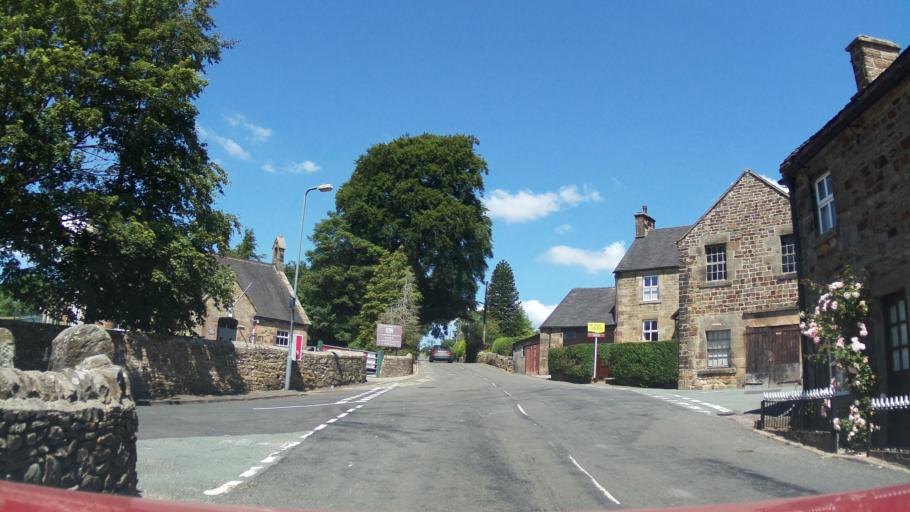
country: GB
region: England
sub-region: Derbyshire
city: Buxton
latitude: 53.1818
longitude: -1.8695
